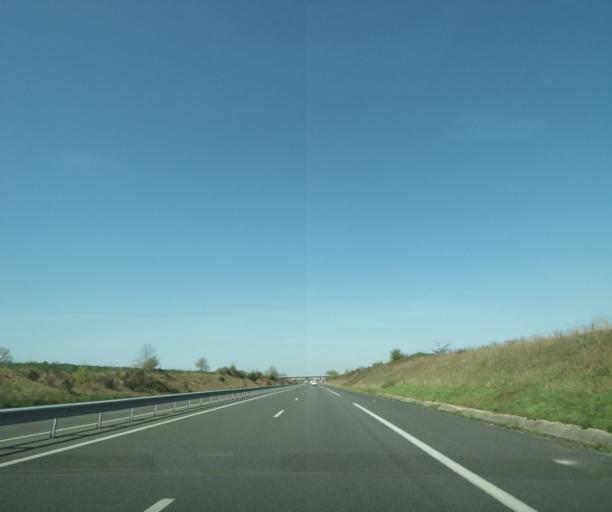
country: FR
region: Auvergne
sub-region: Departement de l'Allier
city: Diou
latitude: 46.5138
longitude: 3.7519
